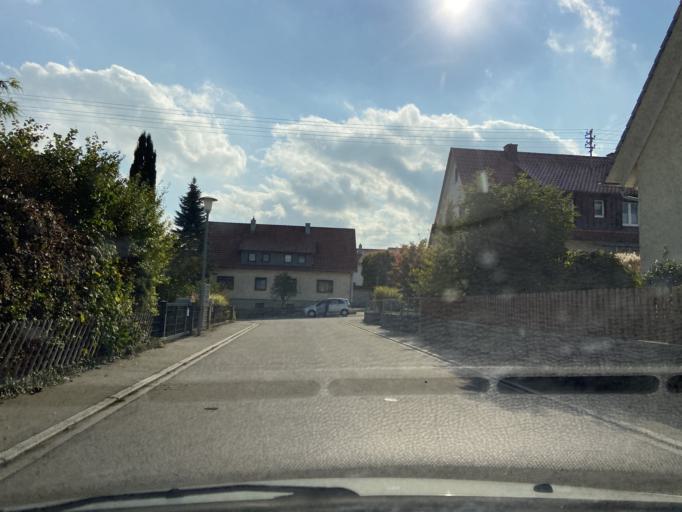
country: DE
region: Baden-Wuerttemberg
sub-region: Tuebingen Region
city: Sigmaringen
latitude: 48.0789
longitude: 9.2192
